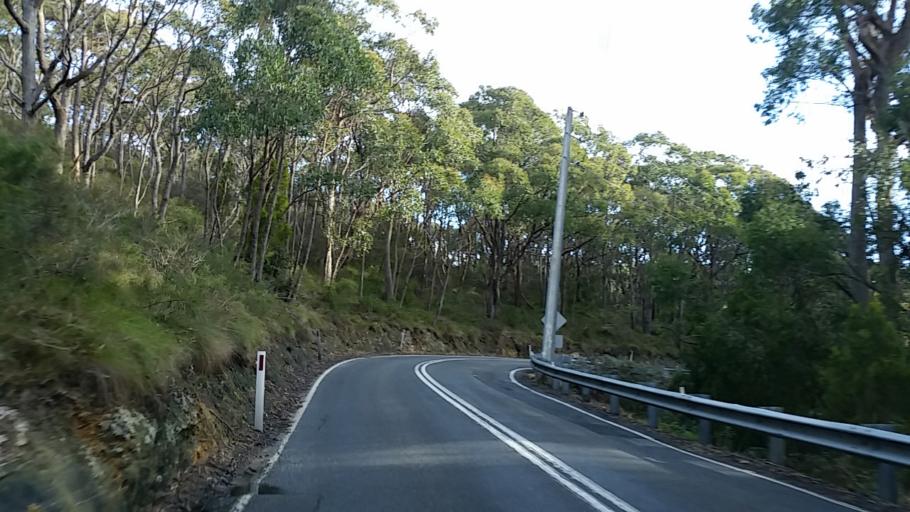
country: AU
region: South Australia
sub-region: Adelaide Hills
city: Bridgewater
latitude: -34.9629
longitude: 138.7550
